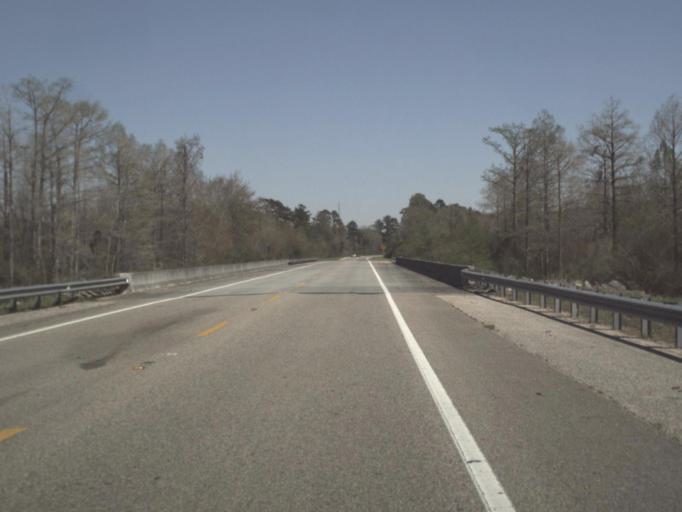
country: US
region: Florida
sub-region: Gadsden County
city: Quincy
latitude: 30.3878
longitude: -84.6666
